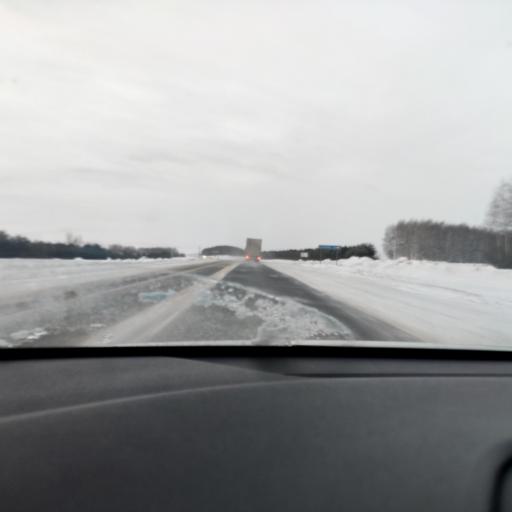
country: RU
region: Tatarstan
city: Sviyazhsk
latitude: 55.6368
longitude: 48.7900
